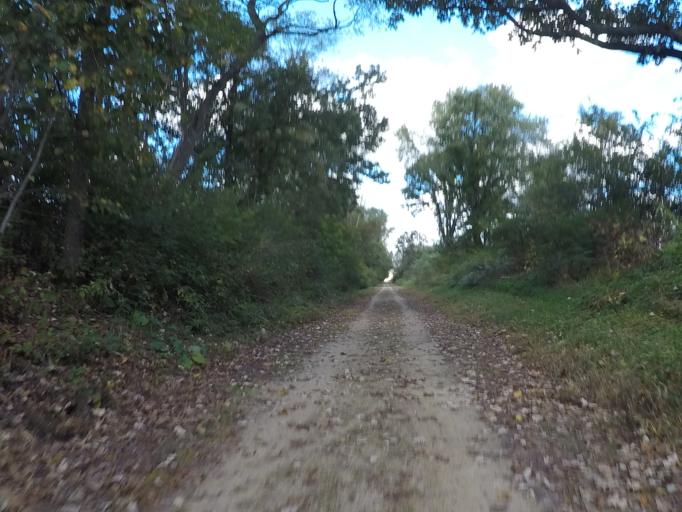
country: US
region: Wisconsin
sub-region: Richland County
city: Richland Center
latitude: 43.3054
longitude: -90.3409
